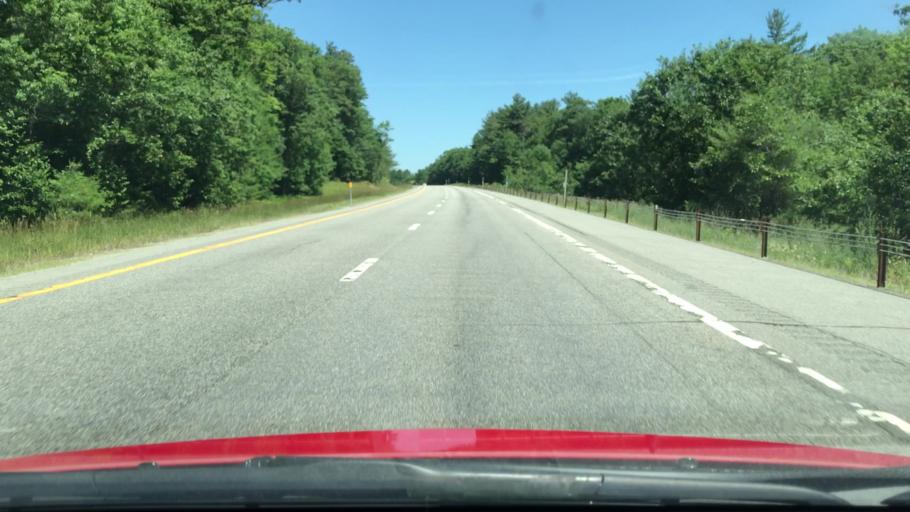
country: US
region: New York
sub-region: Essex County
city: Mineville
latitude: 44.1330
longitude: -73.5875
